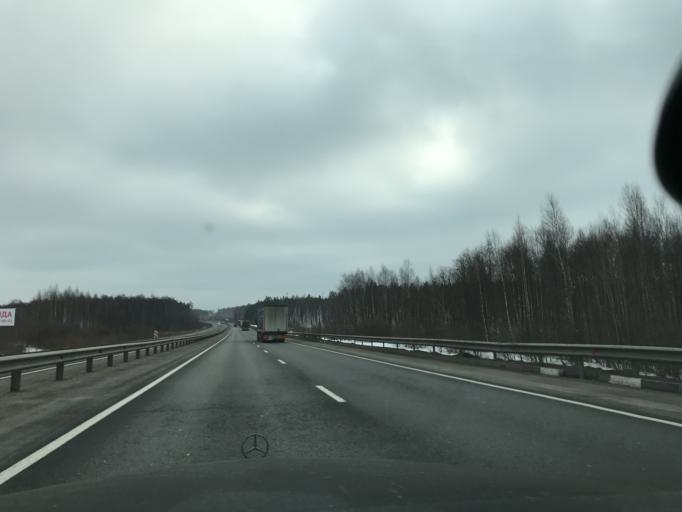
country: RU
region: Vladimir
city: Orgtrud
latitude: 56.1024
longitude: 40.7556
